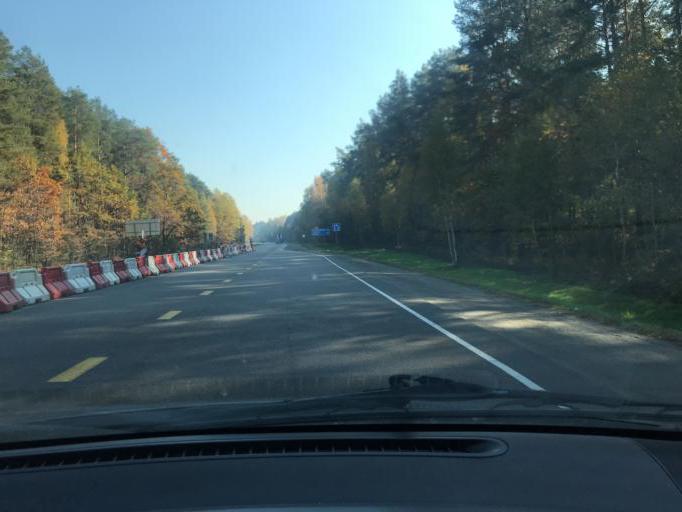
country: BY
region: Brest
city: Luninyets
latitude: 52.2791
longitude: 26.8342
